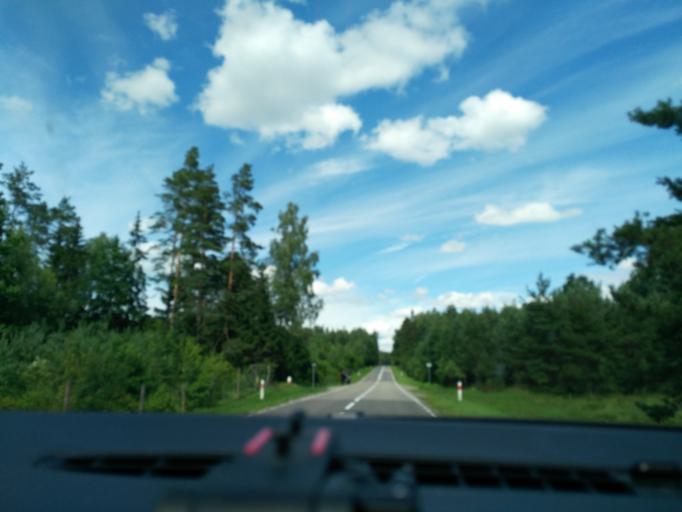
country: PL
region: Podlasie
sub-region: Powiat sejnenski
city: Sejny
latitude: 54.0045
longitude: 23.3198
